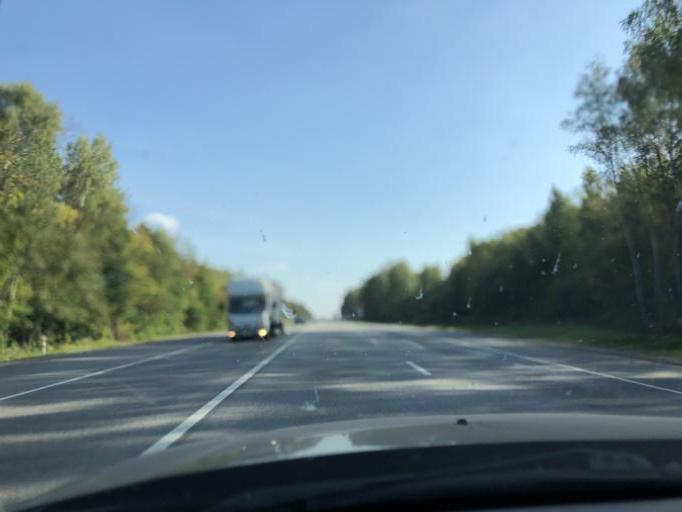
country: RU
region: Tula
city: Leninskiy
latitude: 54.3807
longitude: 37.5165
